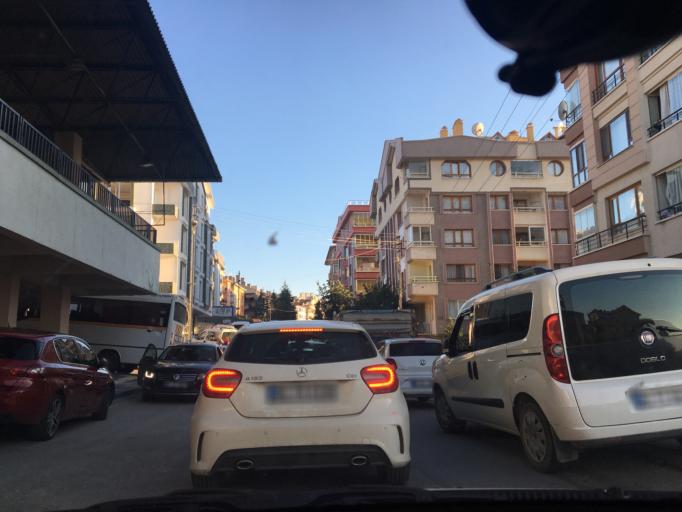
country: TR
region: Ankara
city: Ankara
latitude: 39.8833
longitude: 32.8321
